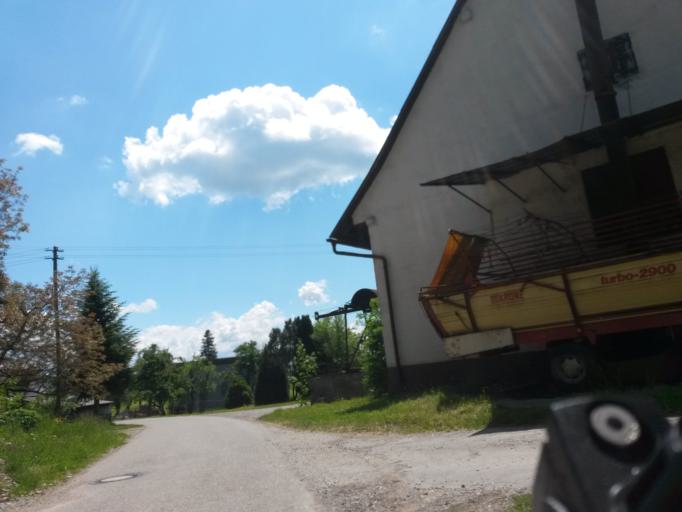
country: DE
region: Baden-Wuerttemberg
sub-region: Tuebingen Region
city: Ingoldingen
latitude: 47.9853
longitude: 9.7134
